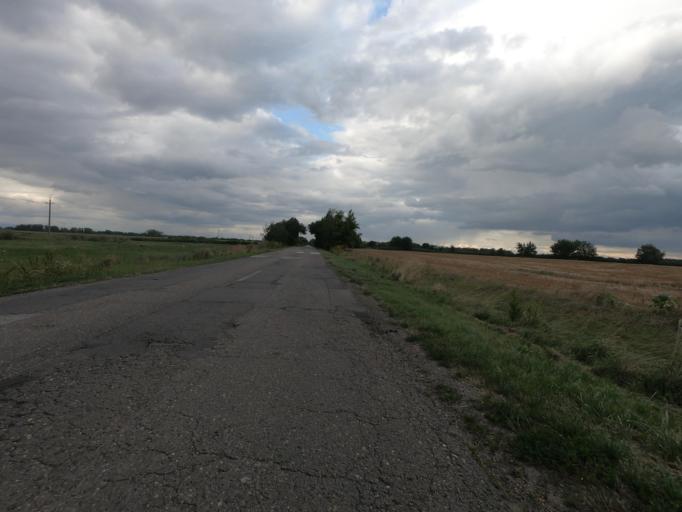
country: HU
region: Heves
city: Poroszlo
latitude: 47.6871
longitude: 20.6522
